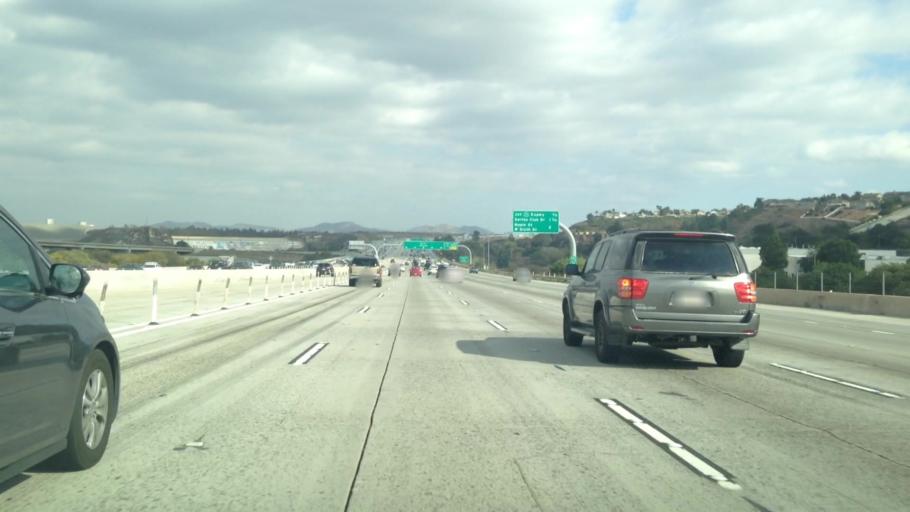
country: US
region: California
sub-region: Riverside County
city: Corona
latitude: 33.8806
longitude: -117.6522
